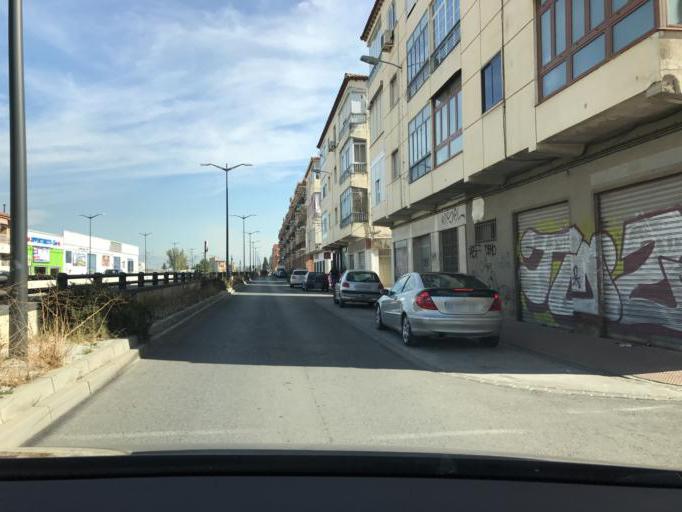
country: ES
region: Andalusia
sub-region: Provincia de Granada
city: Atarfe
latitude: 37.1924
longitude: -3.7165
